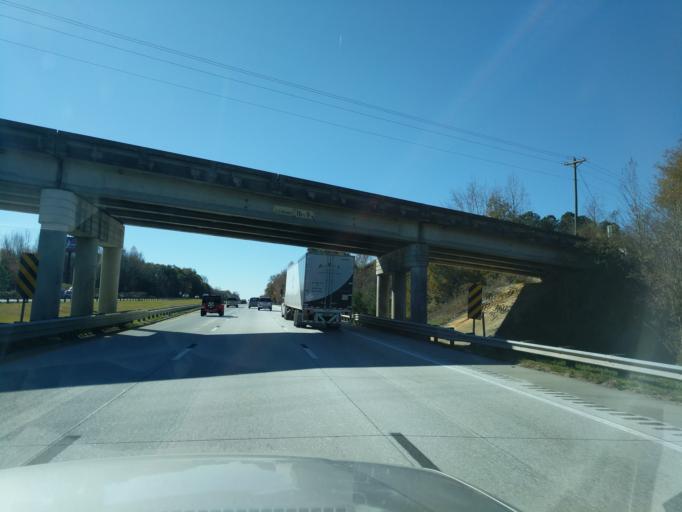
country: US
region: South Carolina
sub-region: Anderson County
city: Williamston
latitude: 34.6648
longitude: -82.5536
